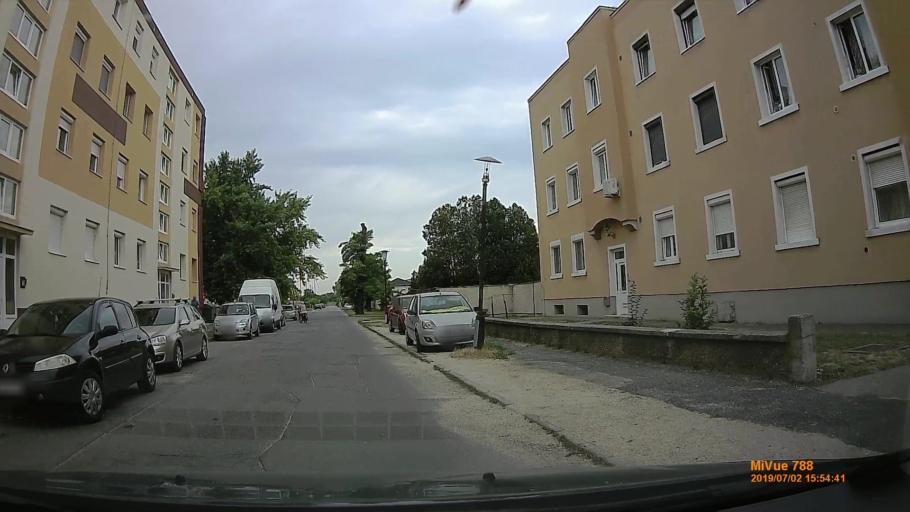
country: HU
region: Gyor-Moson-Sopron
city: Mosonmagyarovar
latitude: 47.8796
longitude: 17.2611
